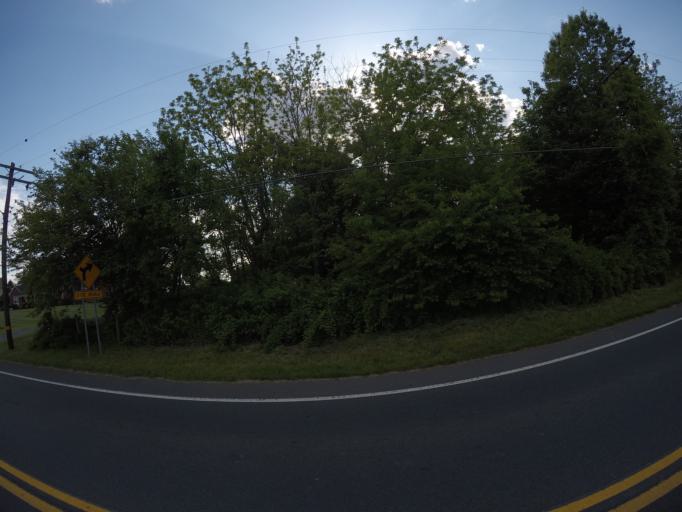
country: US
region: Maryland
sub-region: Montgomery County
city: Damascus
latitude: 39.3021
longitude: -77.1961
